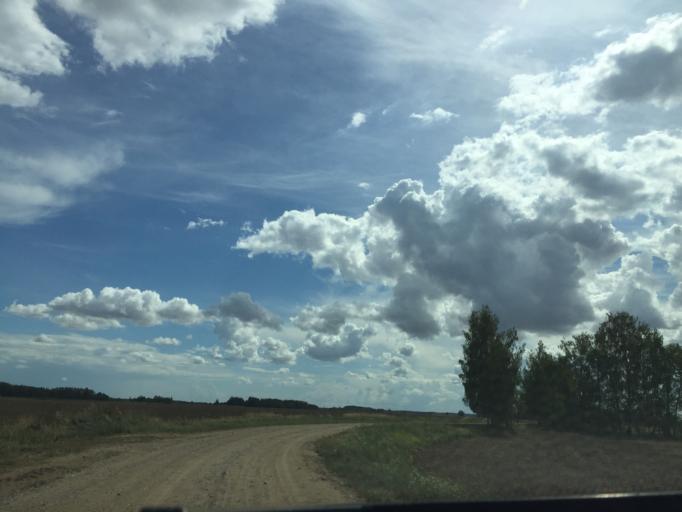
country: LT
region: Siauliu apskritis
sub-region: Joniskis
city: Joniskis
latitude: 56.3556
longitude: 23.6318
